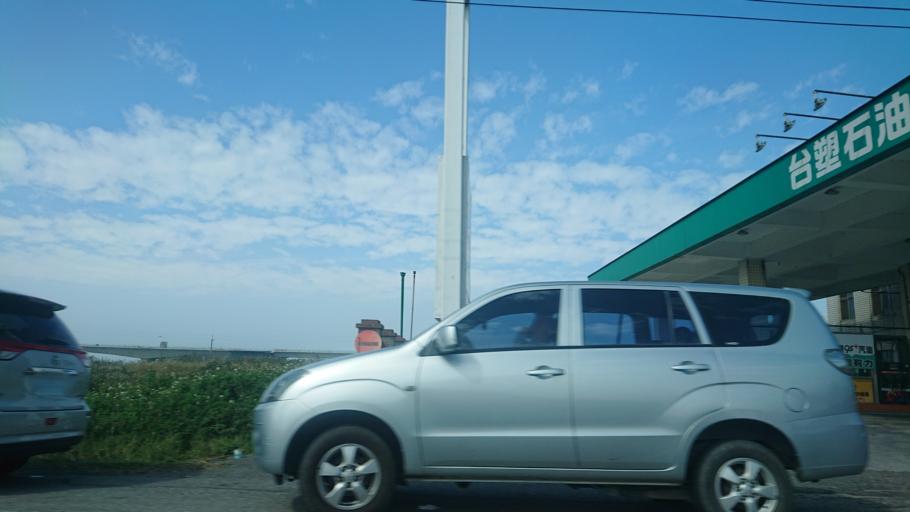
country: TW
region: Taiwan
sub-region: Changhua
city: Chang-hua
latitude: 23.9074
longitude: 120.3089
